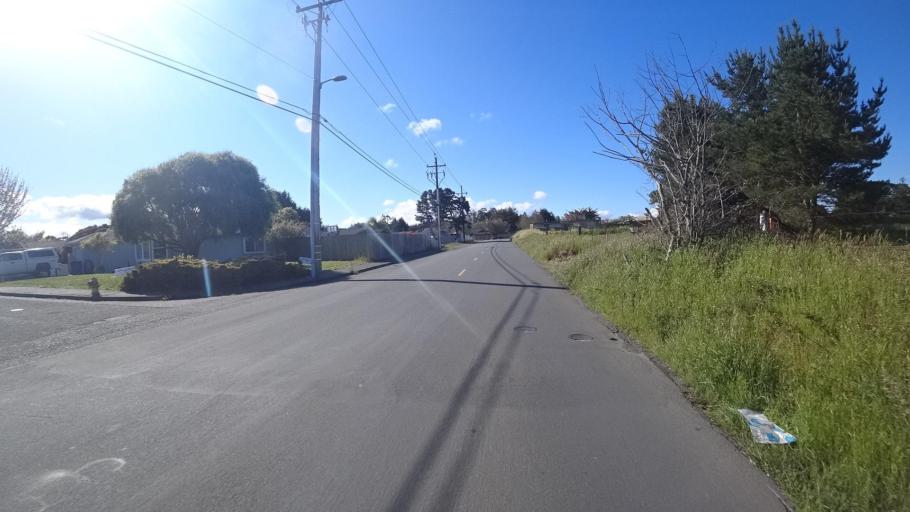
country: US
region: California
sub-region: Humboldt County
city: McKinleyville
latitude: 40.9352
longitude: -124.1070
